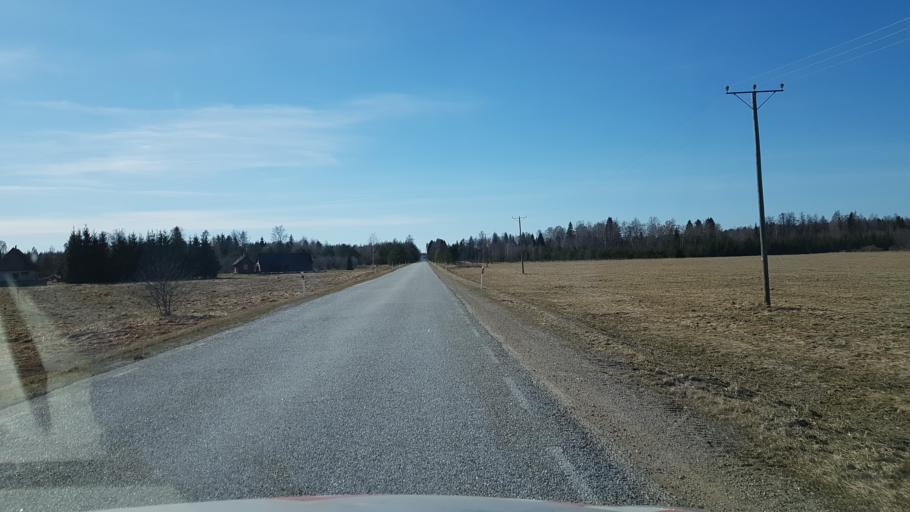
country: EE
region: Ida-Virumaa
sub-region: Kivioli linn
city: Kivioli
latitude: 59.2304
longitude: 26.7739
